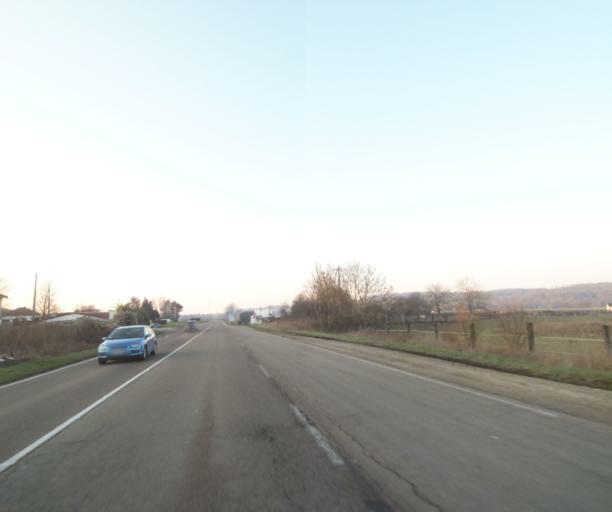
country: FR
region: Champagne-Ardenne
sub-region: Departement de la Haute-Marne
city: Bienville
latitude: 48.6030
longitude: 5.0313
